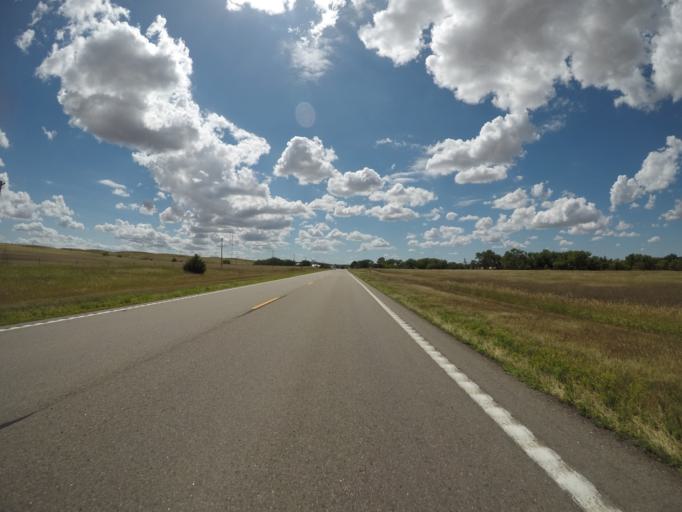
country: US
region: Nebraska
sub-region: Chase County
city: Imperial
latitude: 40.4118
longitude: -101.3556
